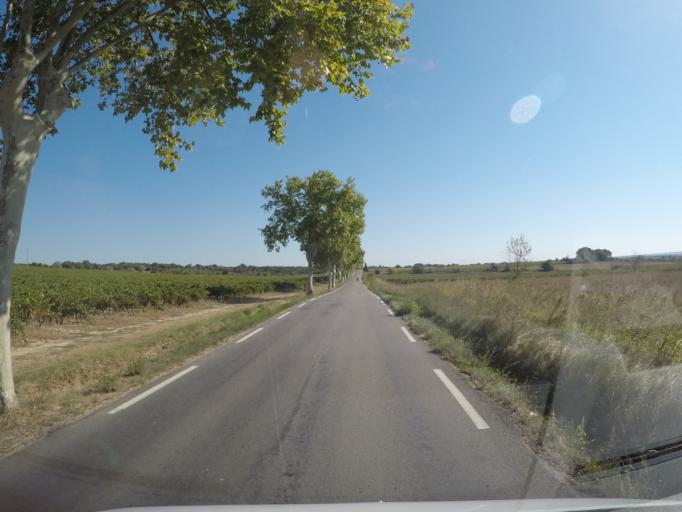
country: FR
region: Languedoc-Roussillon
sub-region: Departement du Gard
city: Saint-Chaptes
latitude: 43.9865
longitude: 4.2760
